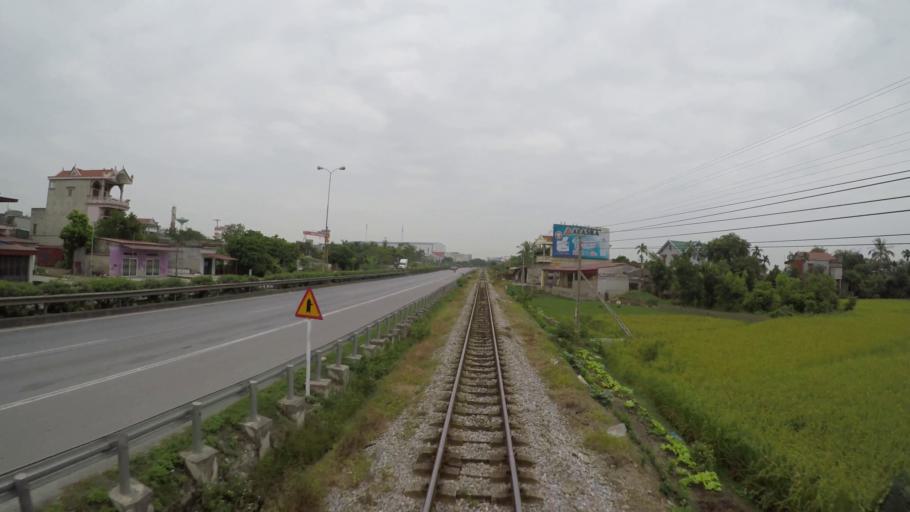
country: VN
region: Hai Duong
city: Phu Thai
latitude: 20.9521
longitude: 106.5315
